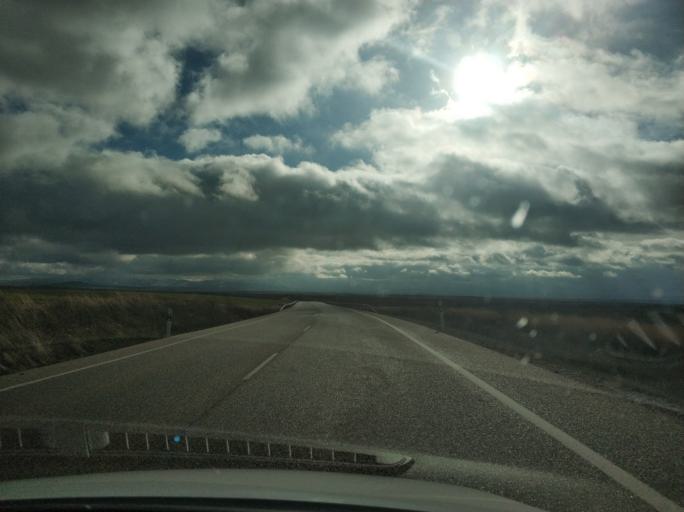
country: ES
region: Castille and Leon
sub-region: Provincia de Segovia
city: Ayllon
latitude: 41.4497
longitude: -3.3409
